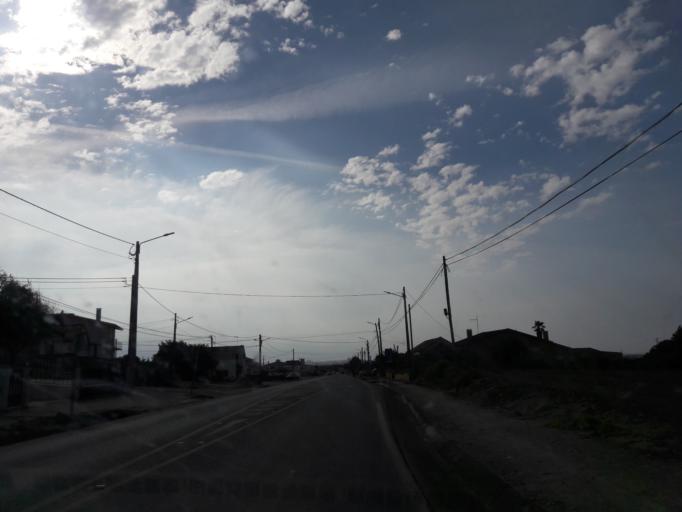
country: PT
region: Leiria
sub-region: Peniche
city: Atouguia da Baleia
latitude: 39.3407
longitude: -9.3309
